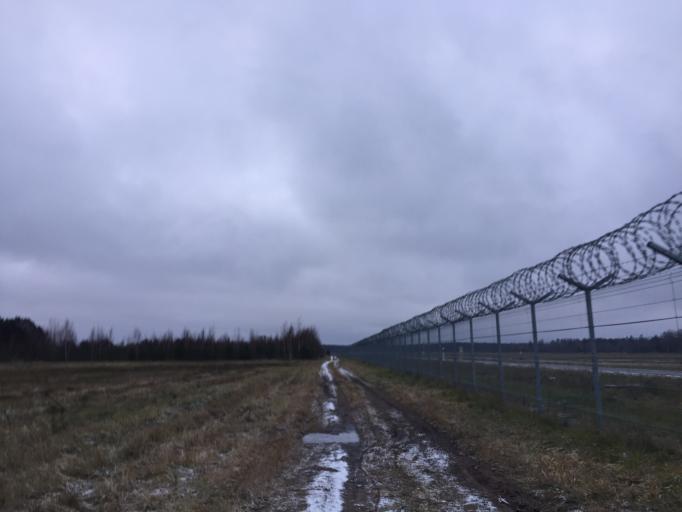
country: LV
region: Babite
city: Pinki
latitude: 56.9069
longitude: 23.9734
